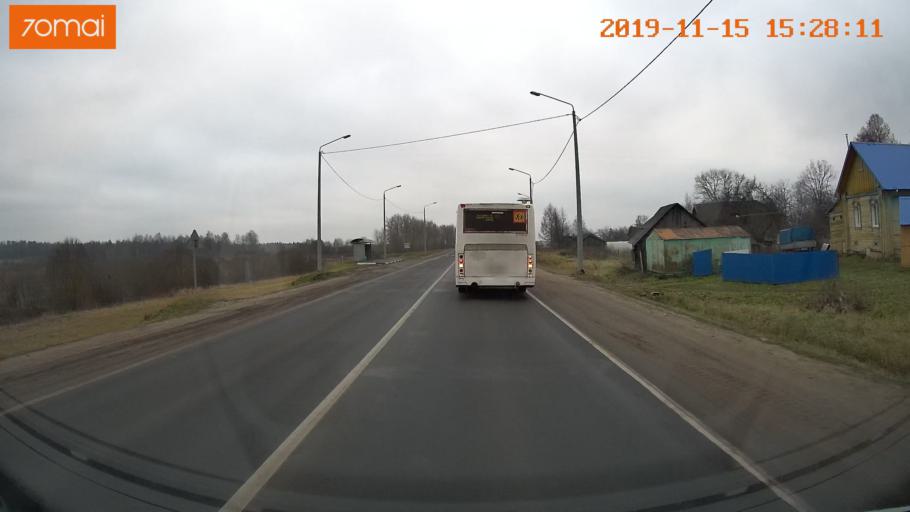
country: RU
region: Jaroslavl
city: Danilov
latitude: 58.1343
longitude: 40.1370
